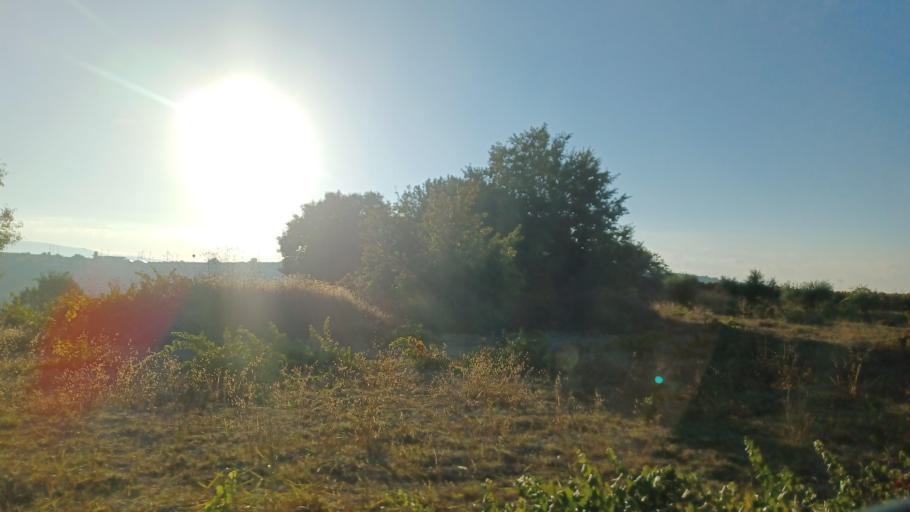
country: CY
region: Pafos
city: Mesogi
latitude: 34.8461
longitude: 32.5162
